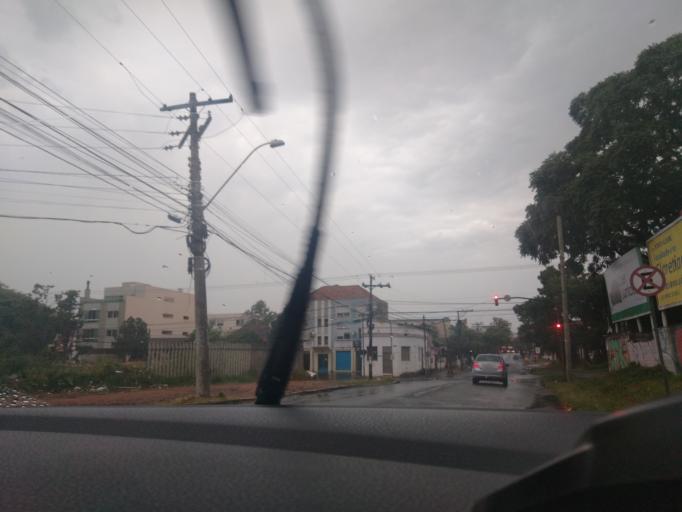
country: BR
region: Rio Grande do Sul
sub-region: Porto Alegre
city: Porto Alegre
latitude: -30.0687
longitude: -51.2080
